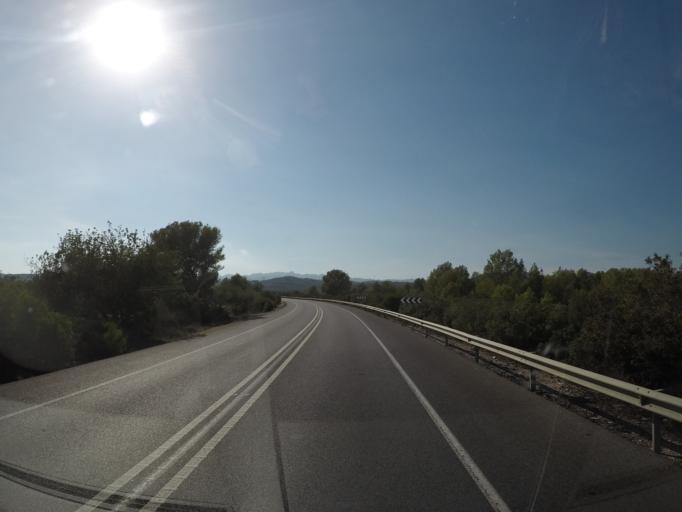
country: ES
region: Catalonia
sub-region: Provincia de Tarragona
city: El Perello
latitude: 40.8978
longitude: 0.7353
